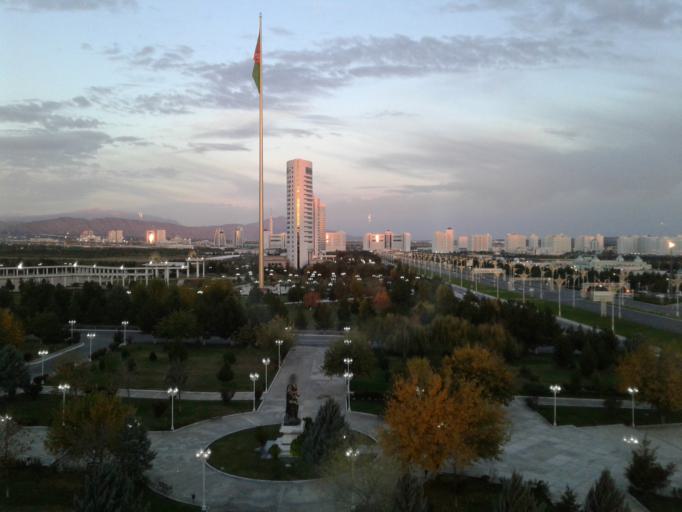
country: TM
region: Ahal
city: Ashgabat
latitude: 37.8862
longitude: 58.3534
